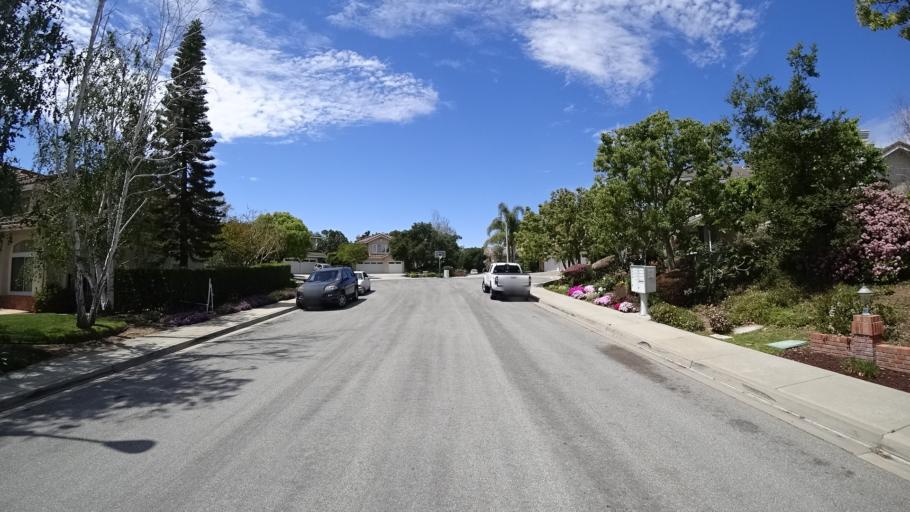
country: US
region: California
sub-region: Ventura County
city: Casa Conejo
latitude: 34.1736
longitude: -118.9165
